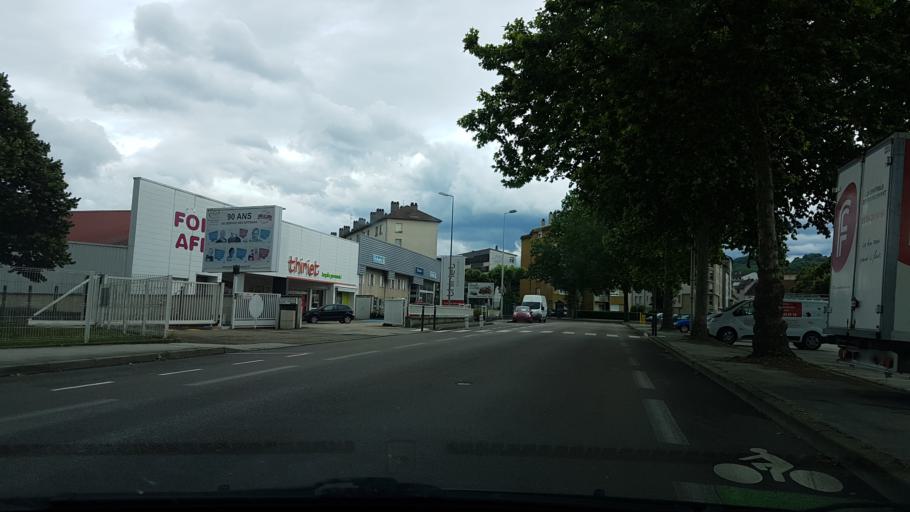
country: FR
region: Franche-Comte
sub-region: Departement du Jura
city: Lons-le-Saunier
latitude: 46.6758
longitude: 5.5437
